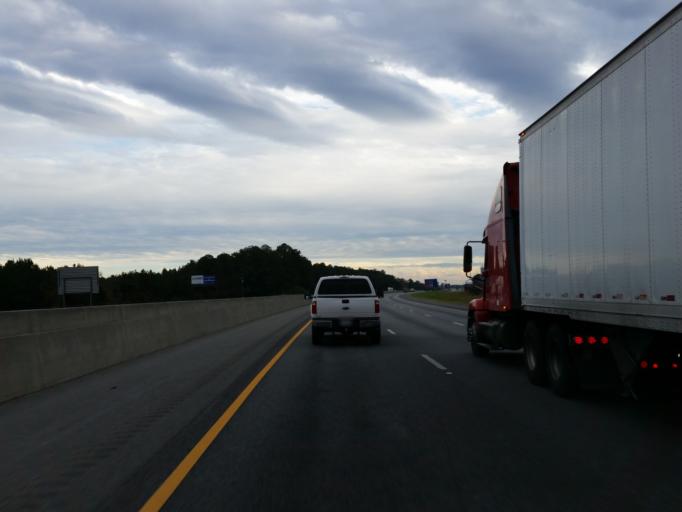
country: US
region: Georgia
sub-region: Lowndes County
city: Remerton
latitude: 30.8734
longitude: -83.3413
